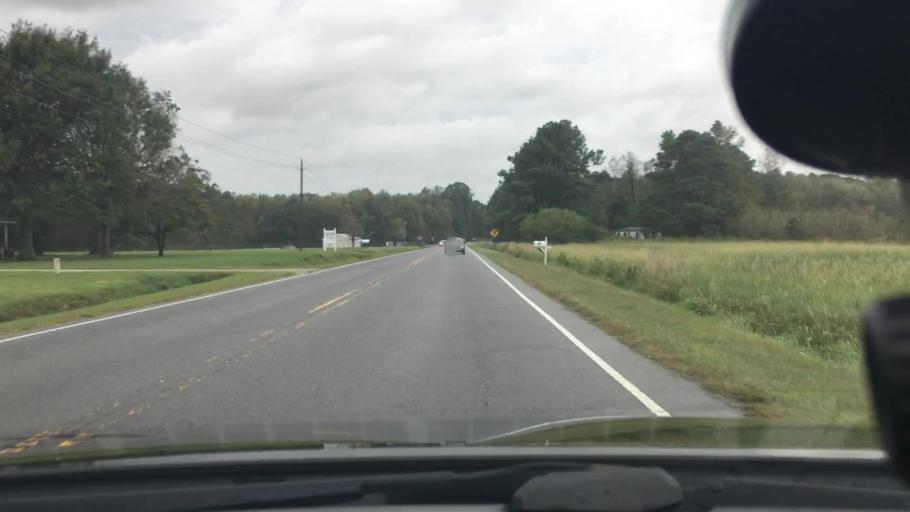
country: US
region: North Carolina
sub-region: Pitt County
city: Windsor
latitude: 35.4321
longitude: -77.2624
